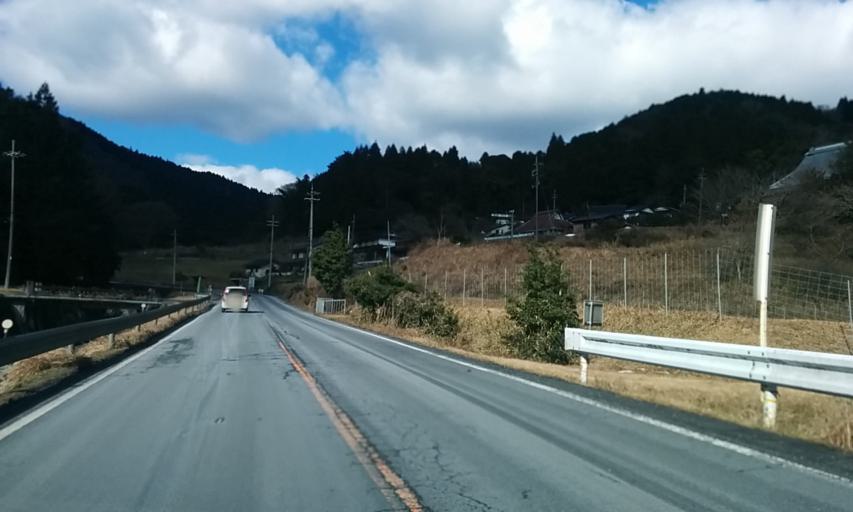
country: JP
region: Kyoto
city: Fukuchiyama
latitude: 35.3811
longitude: 135.0462
